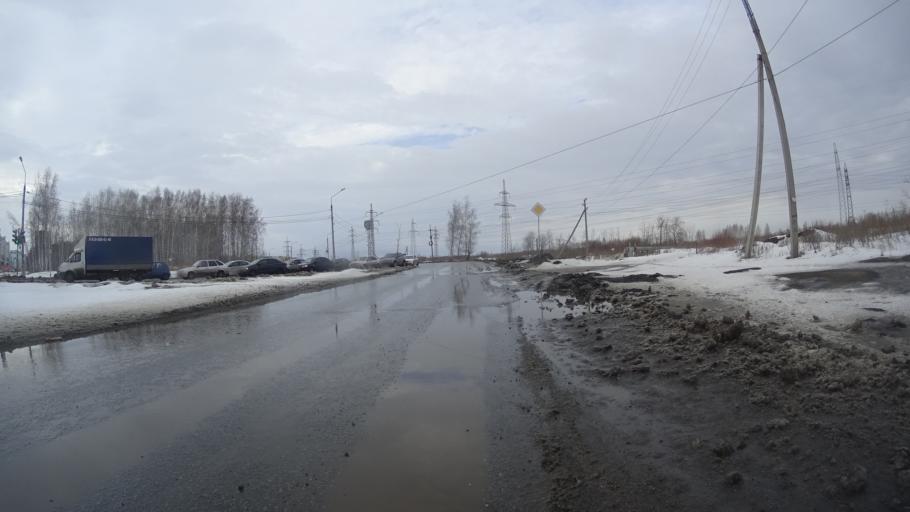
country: RU
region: Chelyabinsk
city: Roshchino
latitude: 55.2084
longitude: 61.3176
